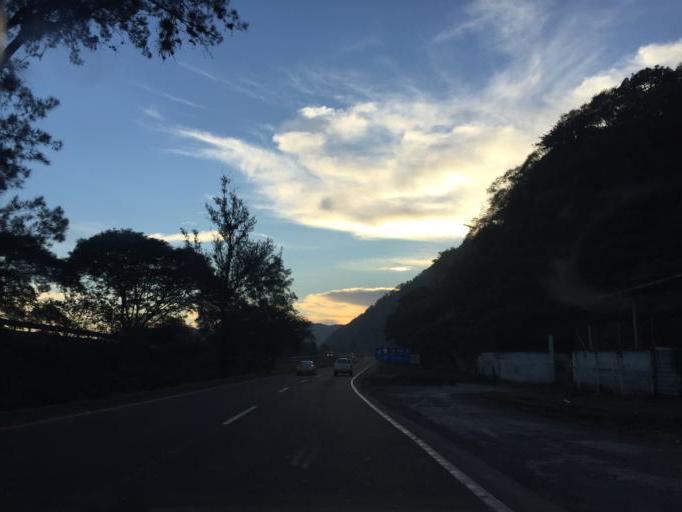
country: MX
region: Veracruz
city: Rio Blanco
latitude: 18.8311
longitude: -97.1274
